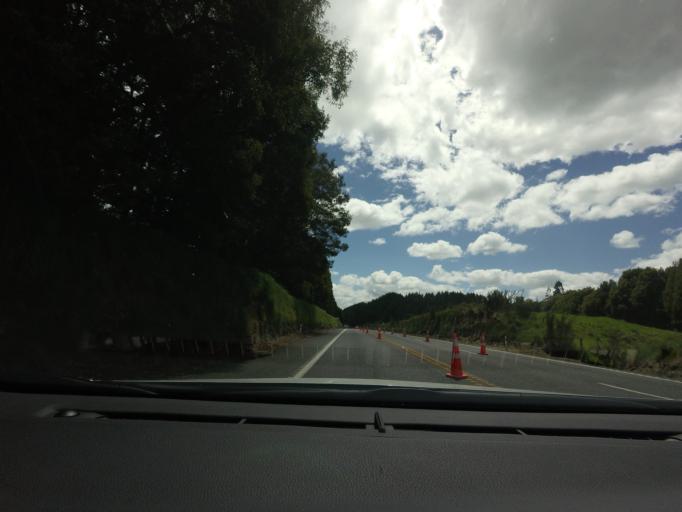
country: NZ
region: Bay of Plenty
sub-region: Rotorua District
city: Rotorua
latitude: -38.2442
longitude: 176.3105
